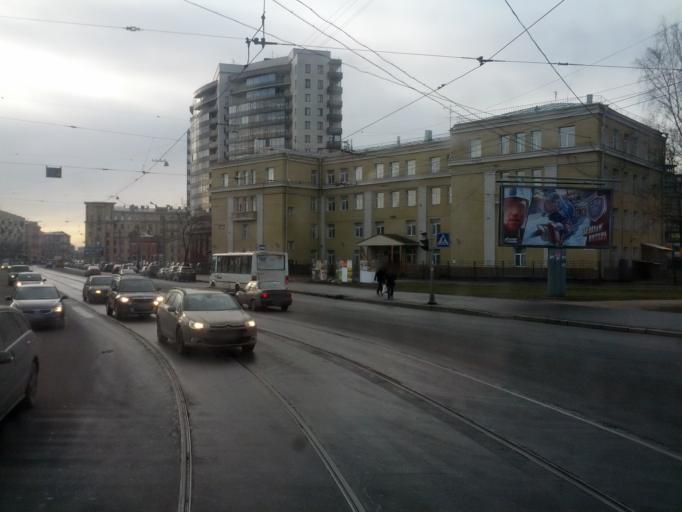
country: RU
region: St.-Petersburg
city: Centralniy
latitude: 59.9338
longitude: 30.4072
